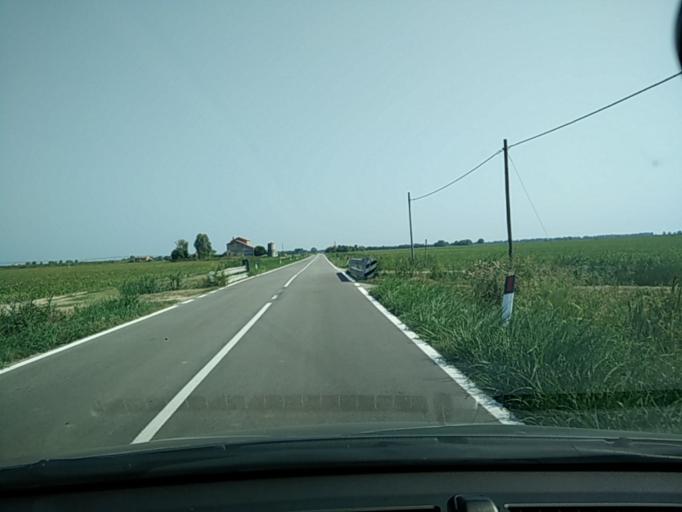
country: IT
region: Veneto
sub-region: Provincia di Venezia
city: La Salute di Livenza
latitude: 45.6431
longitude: 12.8253
